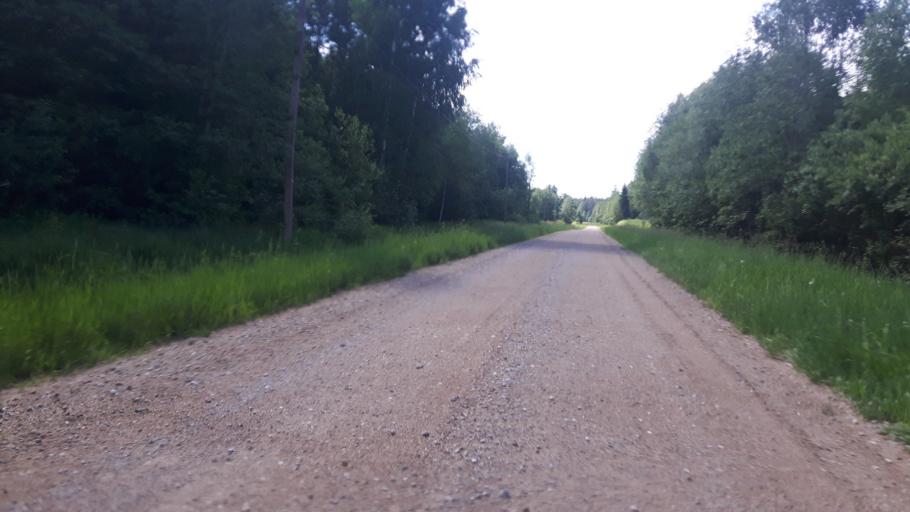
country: EE
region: Paernumaa
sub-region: Vaendra vald (alev)
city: Vandra
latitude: 58.7001
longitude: 25.0296
